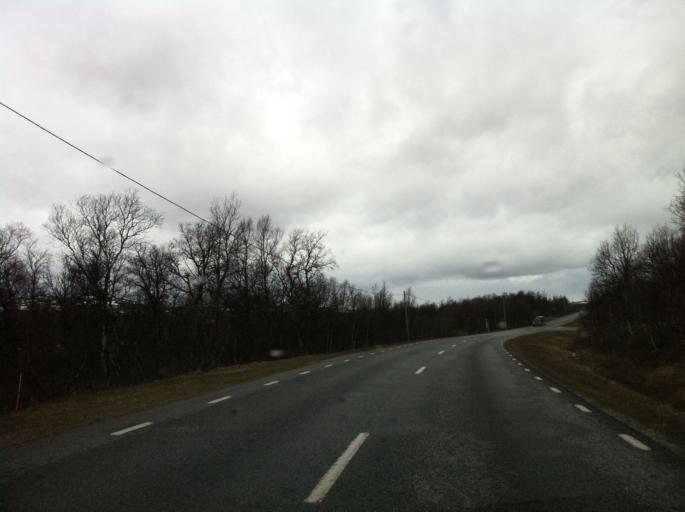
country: NO
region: Sor-Trondelag
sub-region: Tydal
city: Aas
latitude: 62.6015
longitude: 12.1720
